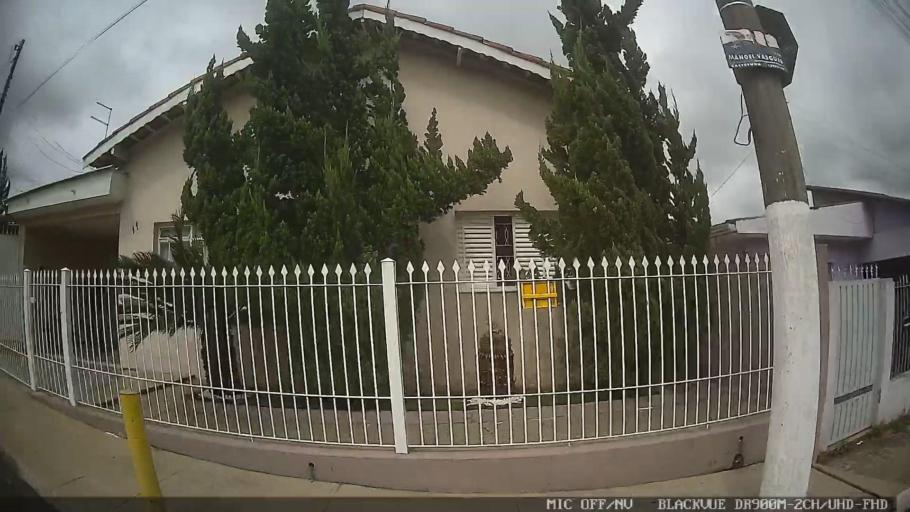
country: BR
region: Sao Paulo
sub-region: Atibaia
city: Atibaia
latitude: -23.1174
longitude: -46.5854
